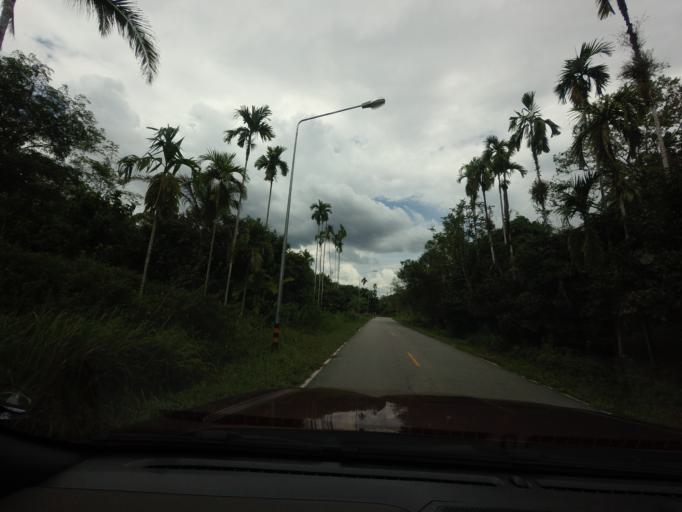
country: TH
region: Narathiwat
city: Sukhirin
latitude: 5.9964
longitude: 101.7006
